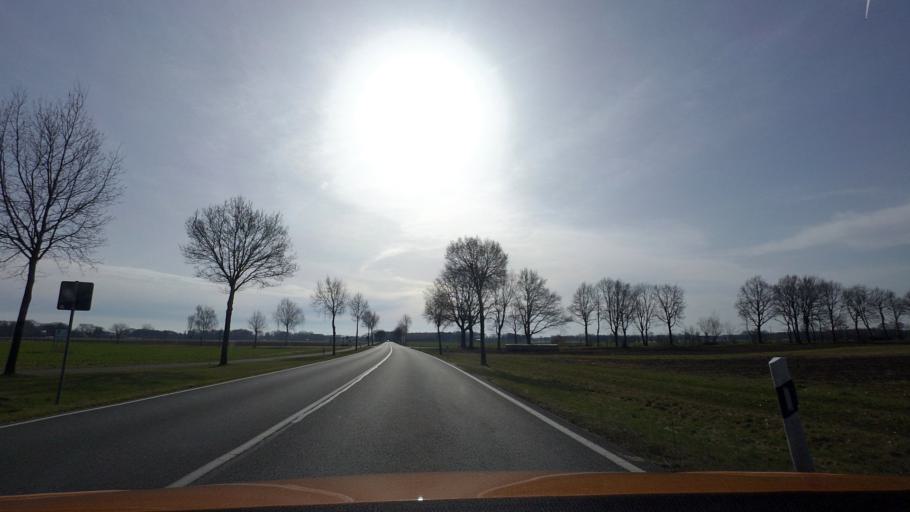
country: DE
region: Lower Saxony
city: Uchte
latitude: 52.4771
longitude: 8.8970
